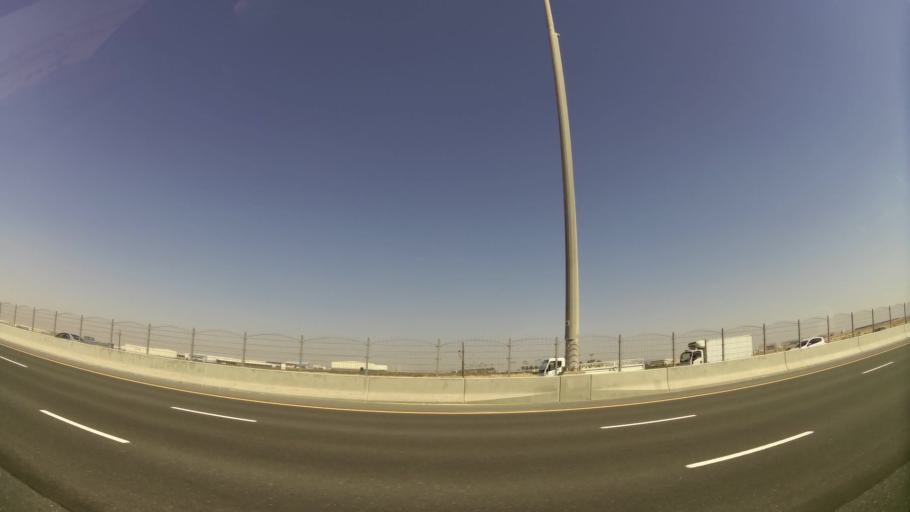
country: AE
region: Dubai
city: Dubai
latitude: 24.9438
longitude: 55.1281
